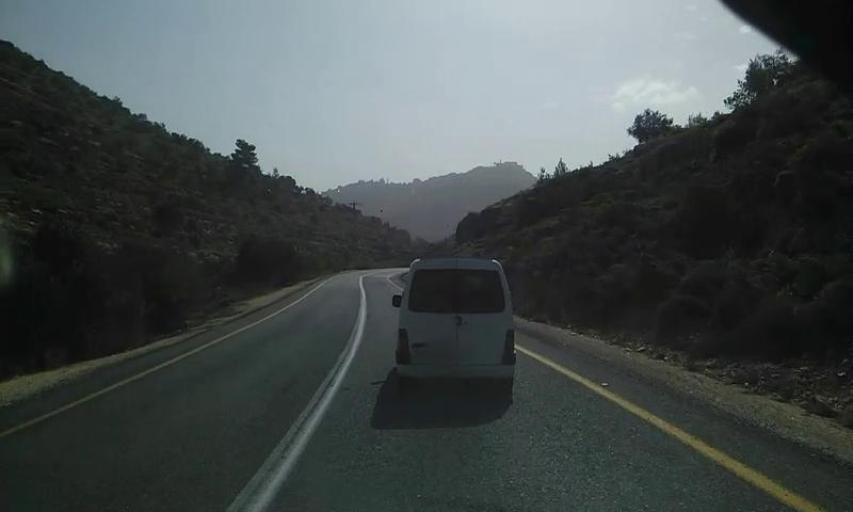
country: PS
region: West Bank
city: Silwad
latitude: 31.9950
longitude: 35.2429
